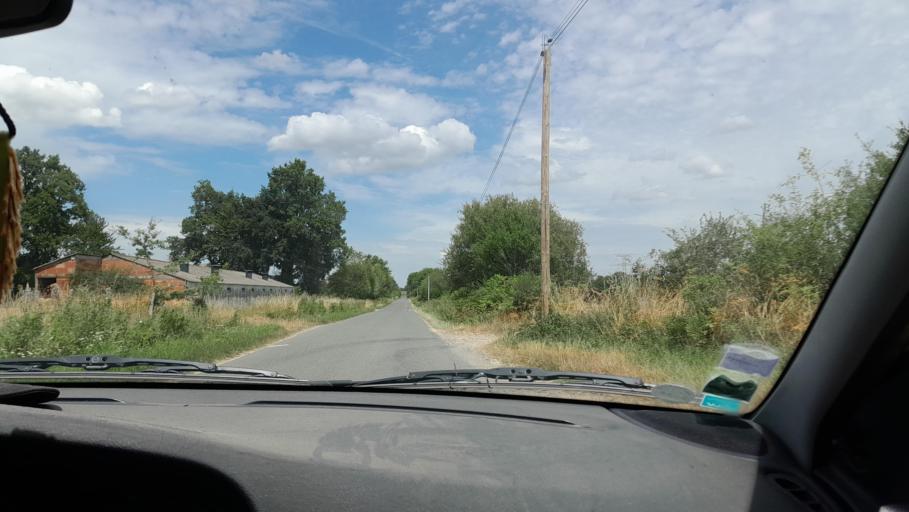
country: FR
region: Pays de la Loire
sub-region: Departement de la Mayenne
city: Saint-Pierre-la-Cour
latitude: 48.1492
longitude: -1.0327
